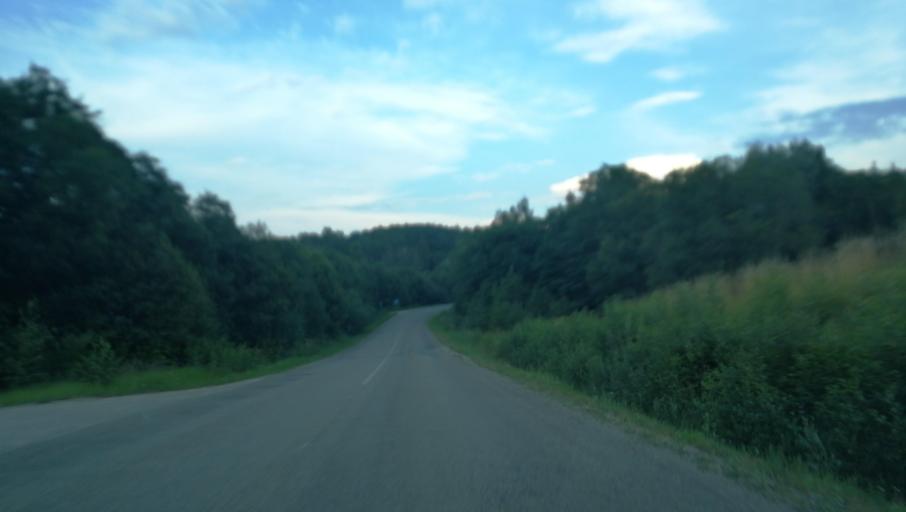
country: LV
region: Priekuli
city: Priekuli
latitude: 57.2594
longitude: 25.3639
